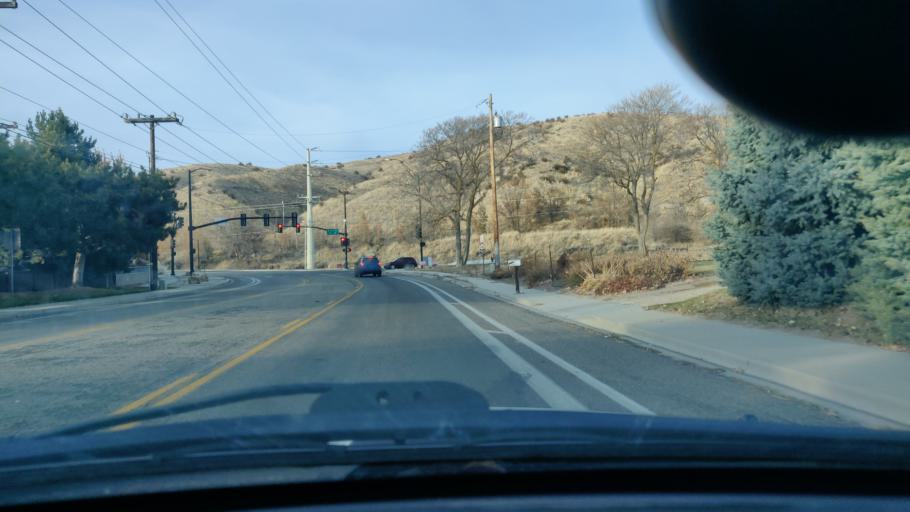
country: US
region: Idaho
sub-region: Ada County
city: Garden City
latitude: 43.6833
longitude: -116.2792
